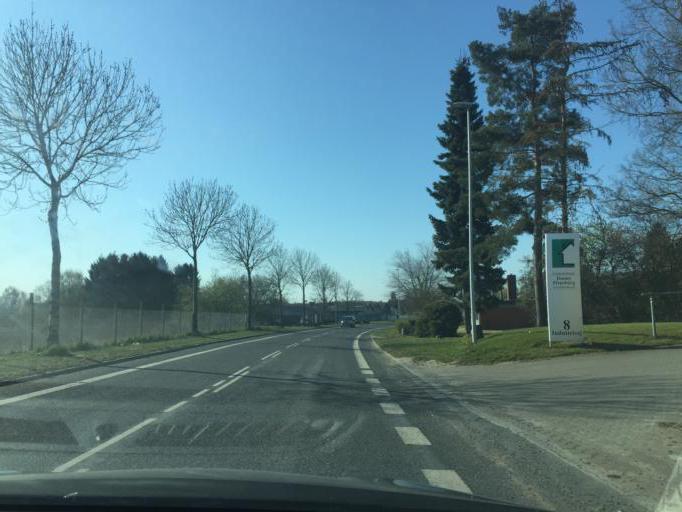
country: DK
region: South Denmark
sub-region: Faaborg-Midtfyn Kommune
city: Ringe
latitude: 55.2481
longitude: 10.4860
